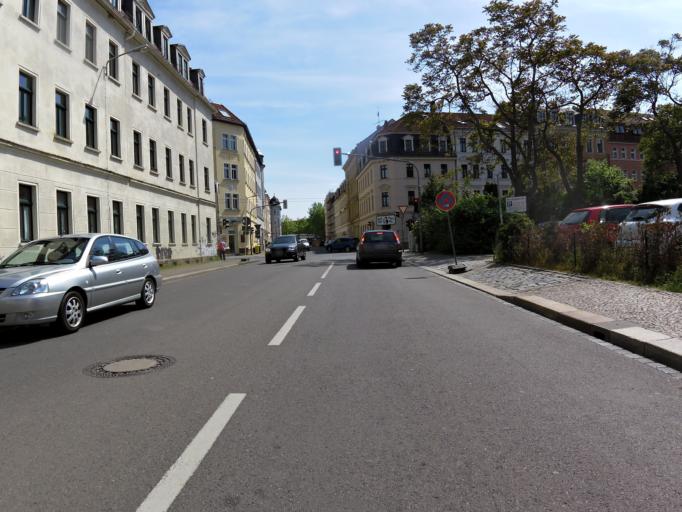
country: DE
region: Saxony
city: Leipzig
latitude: 51.3200
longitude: 12.4220
